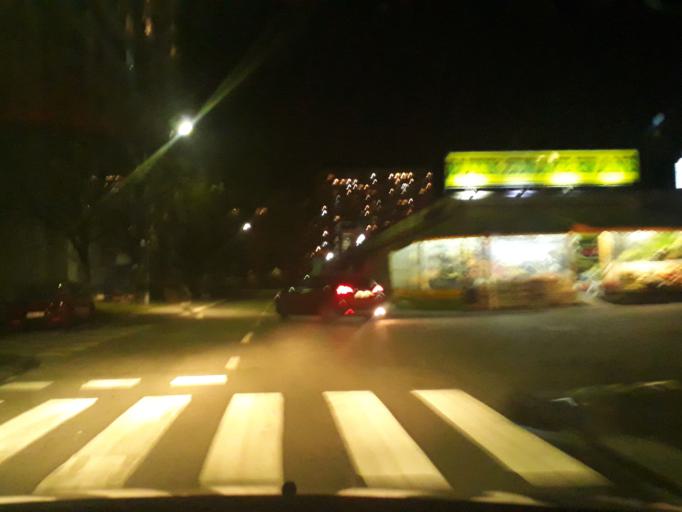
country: BA
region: Federation of Bosnia and Herzegovina
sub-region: Kanton Sarajevo
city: Sarajevo
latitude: 43.8500
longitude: 18.3849
